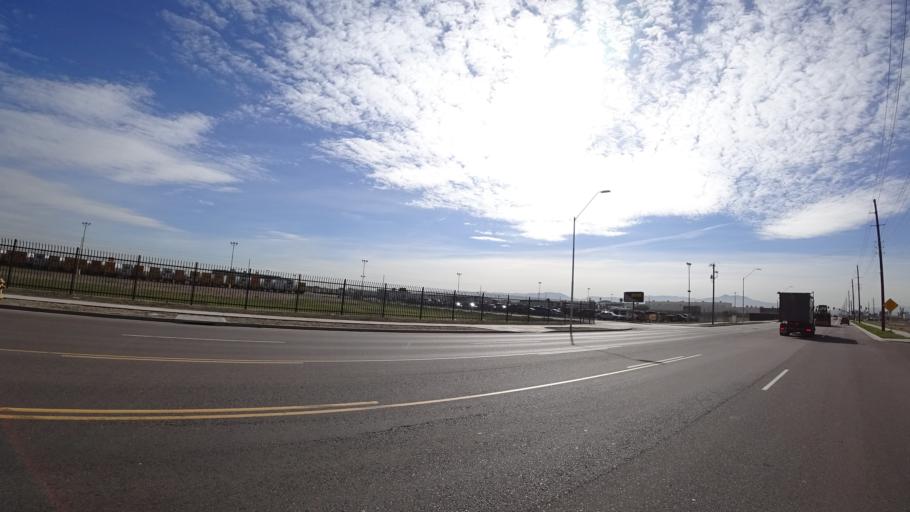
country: US
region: Arizona
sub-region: Maricopa County
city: Laveen
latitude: 33.4250
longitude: -112.1520
